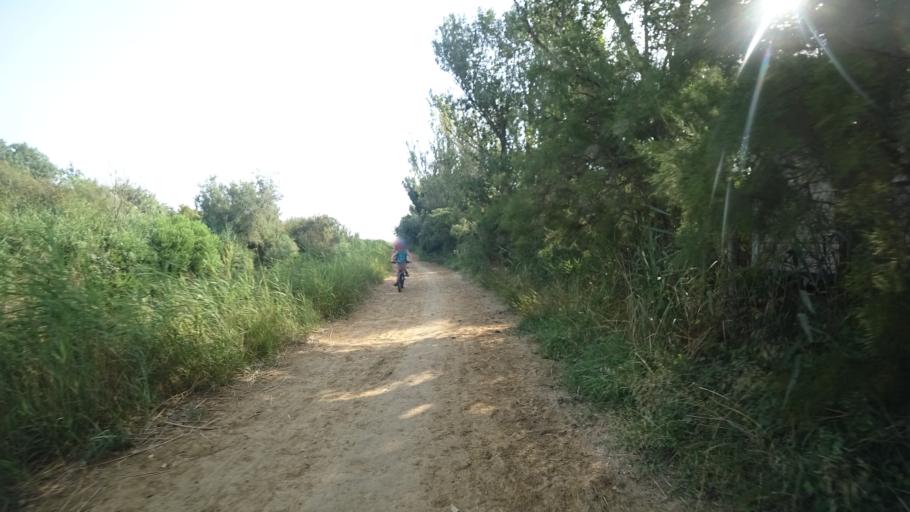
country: FR
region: Languedoc-Roussillon
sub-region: Departement des Pyrenees-Orientales
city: Sainte-Marie-Plage
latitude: 42.7408
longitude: 3.0322
